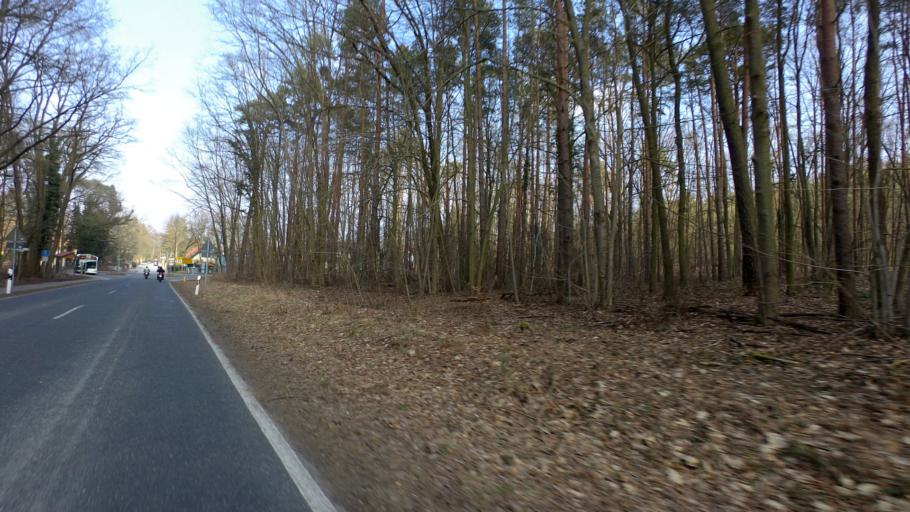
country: DE
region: Brandenburg
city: Werder
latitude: 52.3363
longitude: 12.9724
